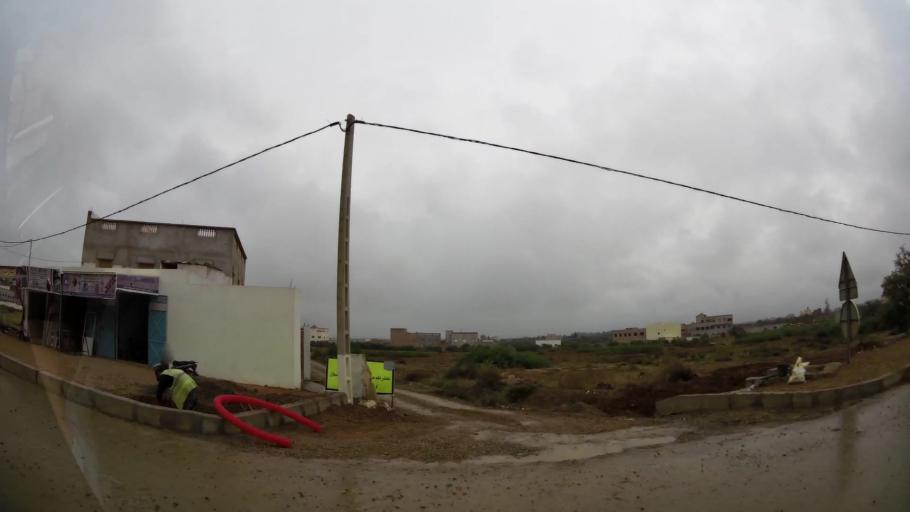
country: MA
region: Taza-Al Hoceima-Taounate
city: Imzourene
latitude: 35.1604
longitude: -3.8543
